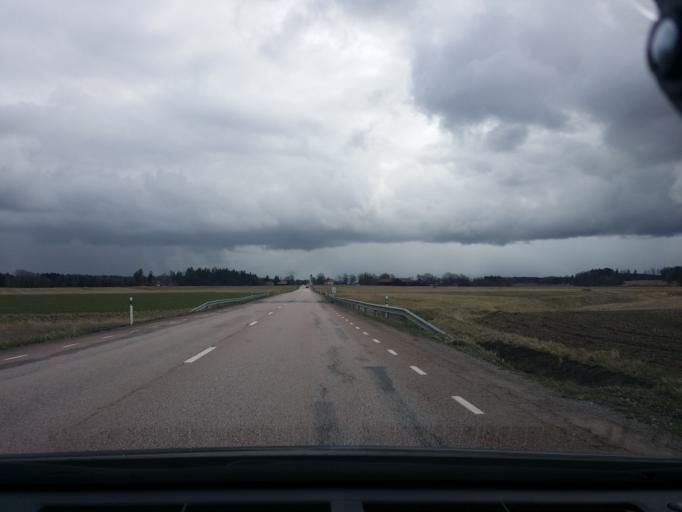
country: SE
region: Uppsala
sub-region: Enkopings Kommun
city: Irsta
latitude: 59.7765
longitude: 16.8686
